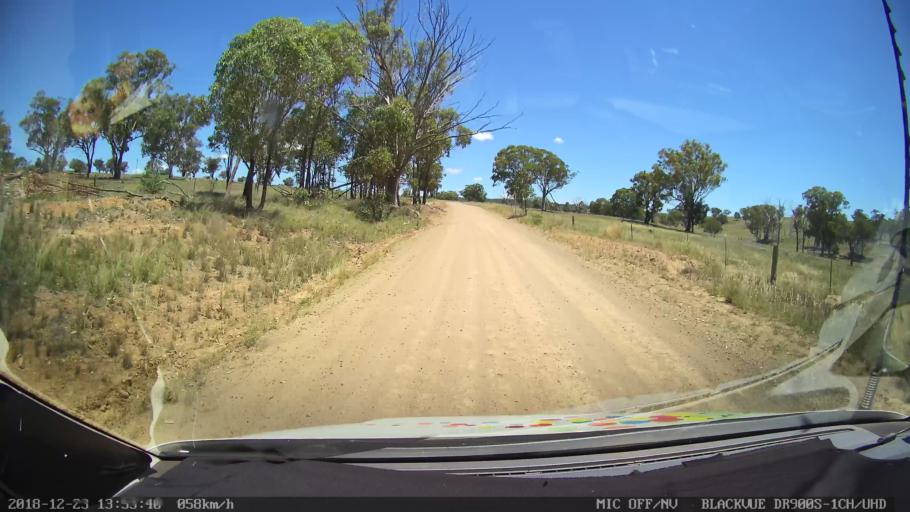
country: AU
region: New South Wales
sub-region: Tamworth Municipality
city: Manilla
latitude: -30.5542
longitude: 151.0929
